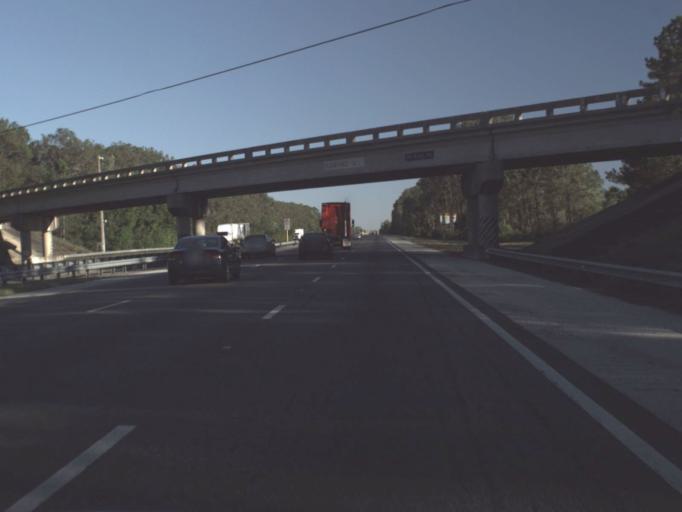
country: US
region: Florida
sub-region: Flagler County
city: Palm Coast
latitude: 29.6379
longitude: -81.2691
